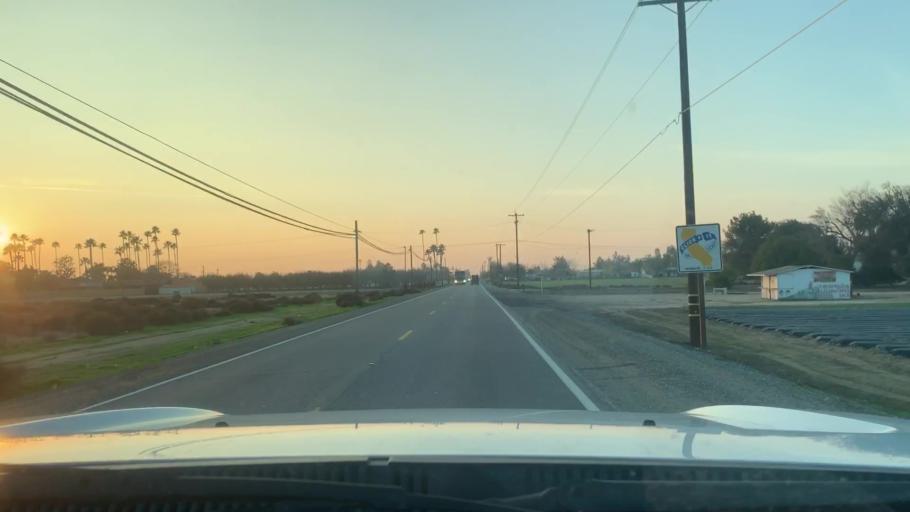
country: US
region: California
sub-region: Kern County
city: Rosedale
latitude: 35.3835
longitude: -119.1865
